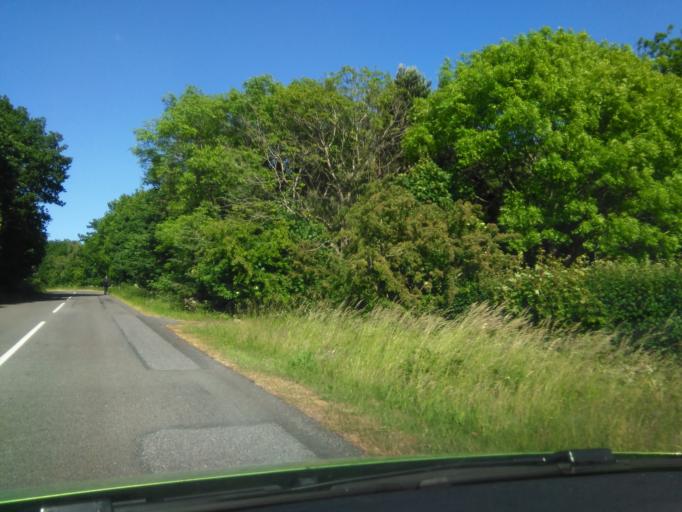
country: DK
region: Capital Region
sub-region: Bornholm Kommune
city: Nexo
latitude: 55.0654
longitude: 15.0813
